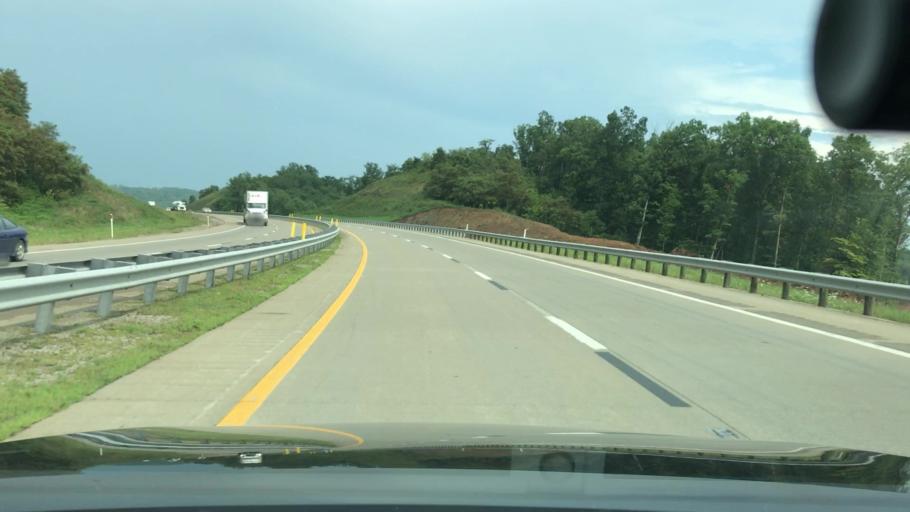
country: US
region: West Virginia
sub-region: Mason County
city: Point Pleasant
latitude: 38.7640
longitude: -82.0193
